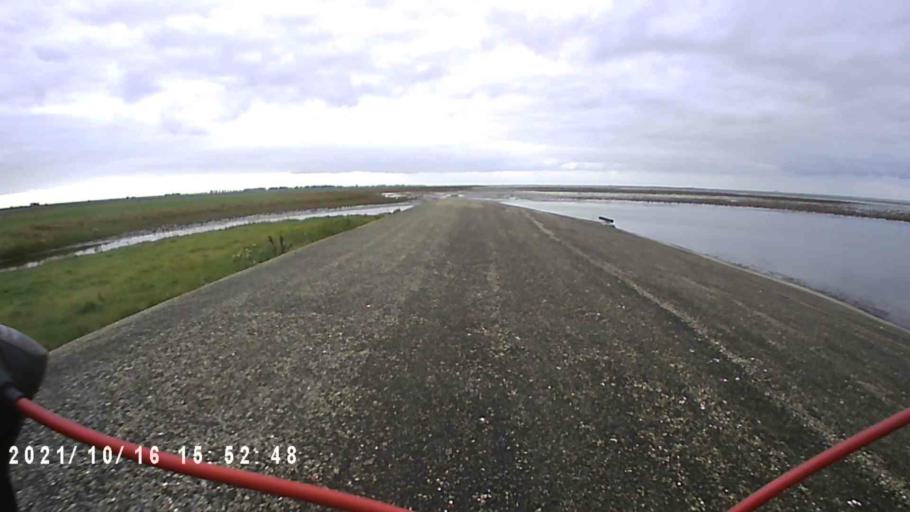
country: NL
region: Friesland
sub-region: Gemeente Dongeradeel
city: Anjum
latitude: 53.4052
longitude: 6.1251
